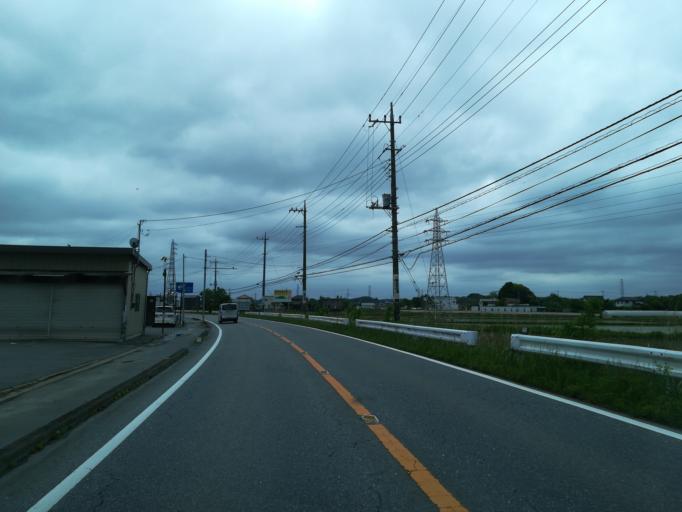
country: JP
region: Ibaraki
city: Tsukuba
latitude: 36.1826
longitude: 140.0790
